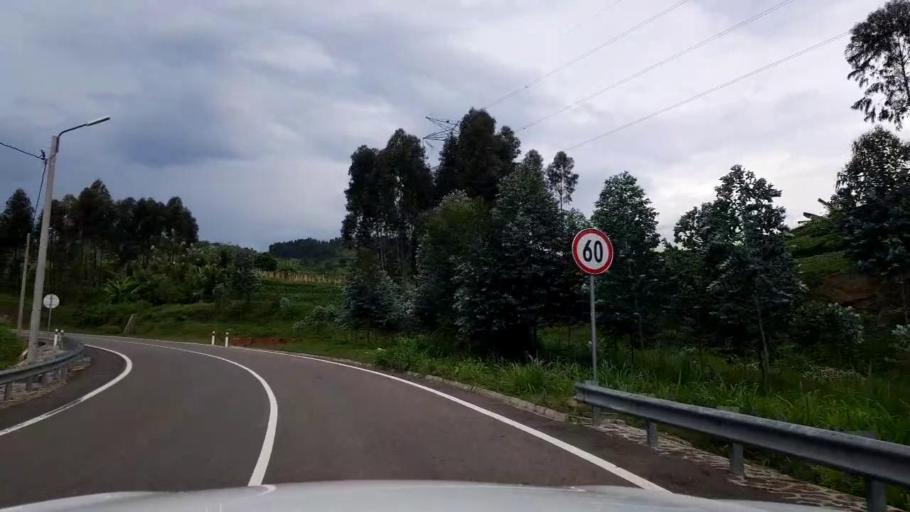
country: RW
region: Western Province
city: Kibuye
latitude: -2.0316
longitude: 29.3971
